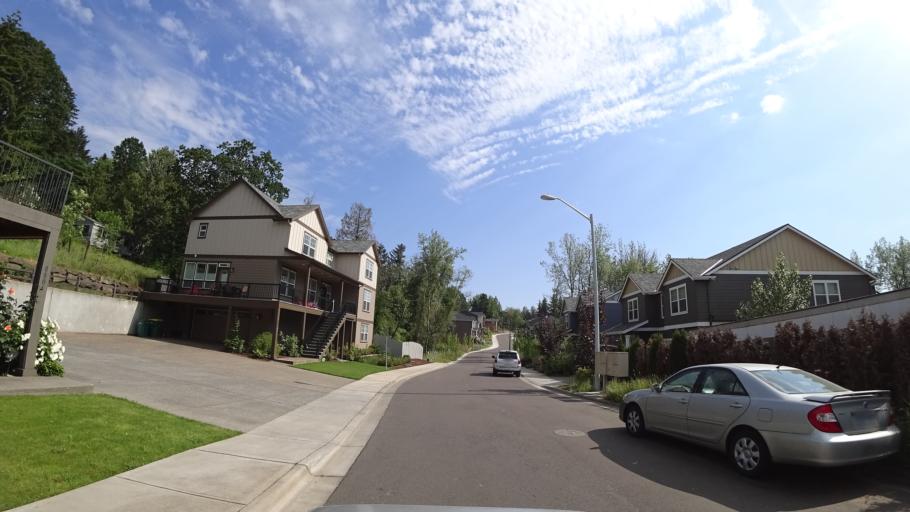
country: US
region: Oregon
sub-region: Washington County
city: Garden Home-Whitford
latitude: 45.4562
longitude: -122.7509
